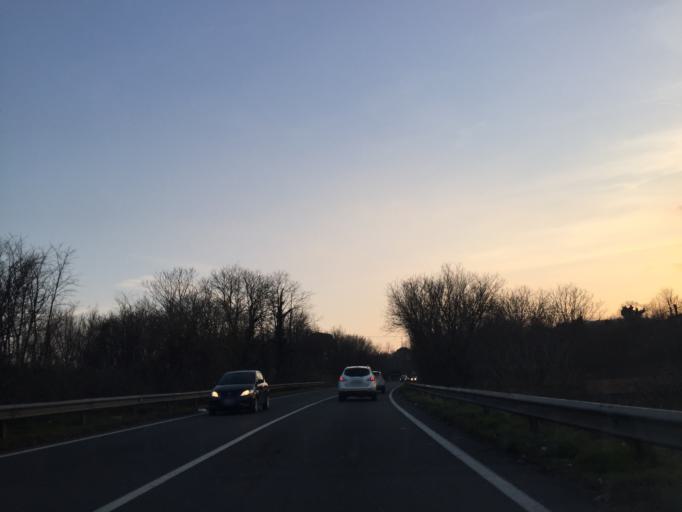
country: IT
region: Campania
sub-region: Provincia di Avellino
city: Avellino
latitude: 40.9056
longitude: 14.8090
